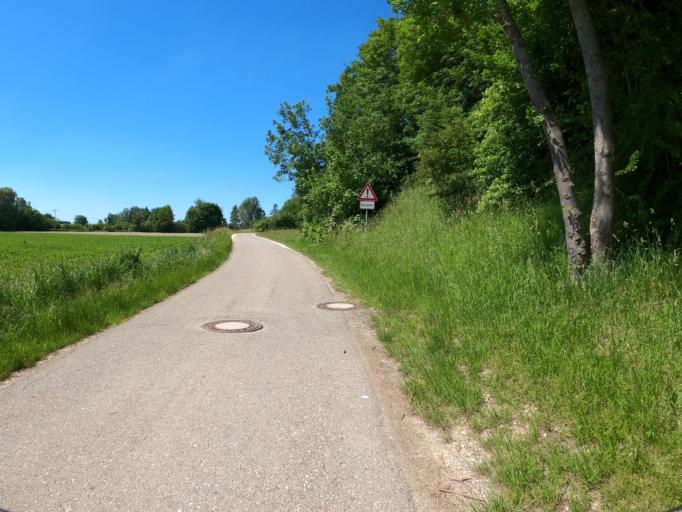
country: DE
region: Bavaria
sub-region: Swabia
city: Pfaffenhofen an der Roth
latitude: 48.3719
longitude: 10.1518
